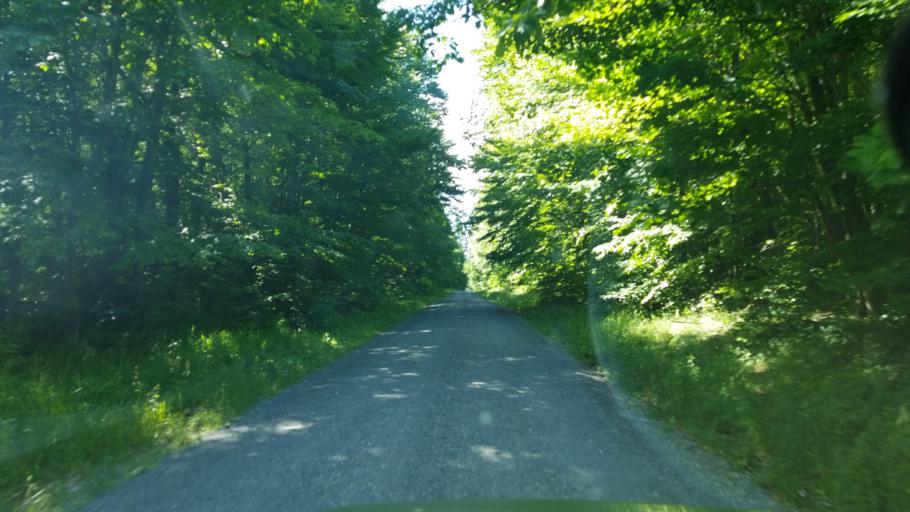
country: US
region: Pennsylvania
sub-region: Clearfield County
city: Clearfield
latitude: 41.2051
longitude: -78.4887
